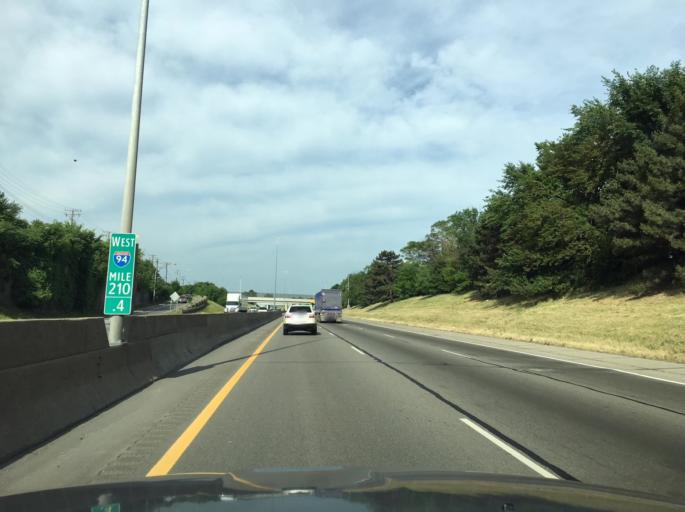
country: US
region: Michigan
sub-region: Wayne County
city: Dearborn
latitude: 42.3301
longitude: -83.1513
